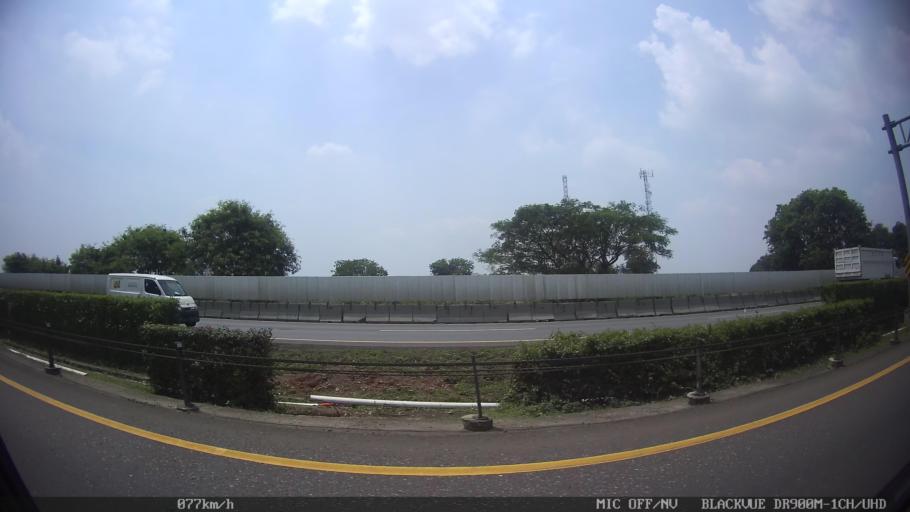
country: ID
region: Banten
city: Serang
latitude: -6.1391
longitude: 106.2606
